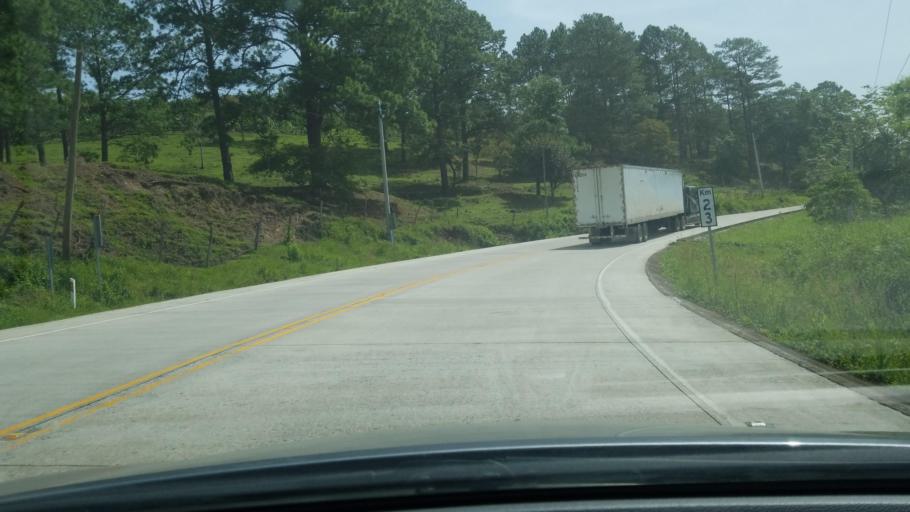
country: HN
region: Copan
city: San Jeronimo
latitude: 14.9713
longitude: -88.8909
